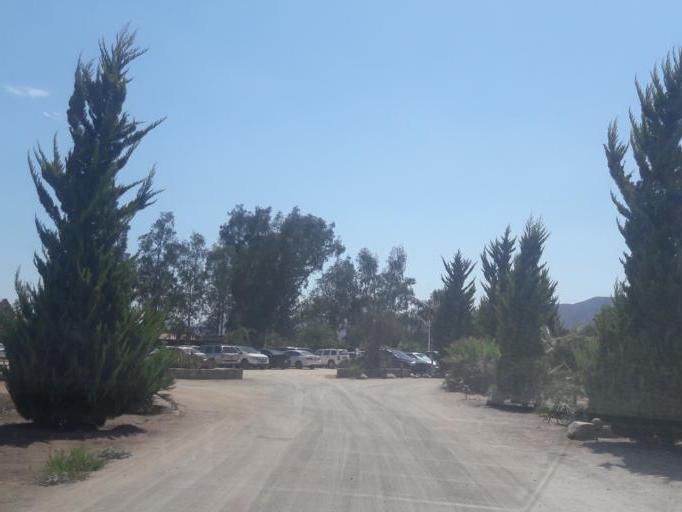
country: MX
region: Baja California
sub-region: Ensenada
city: Rancho Verde
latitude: 32.0995
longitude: -116.6212
